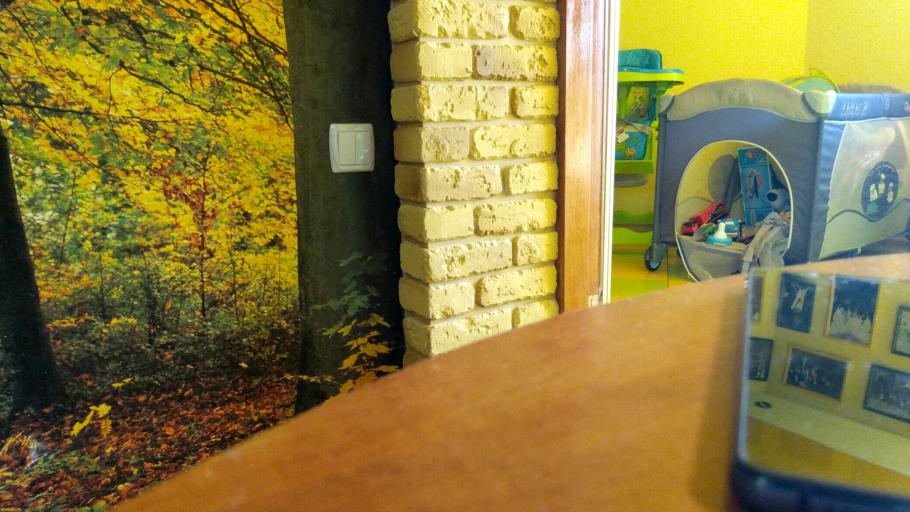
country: RU
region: Tverskaya
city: Likhoslavl'
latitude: 57.2663
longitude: 35.3990
